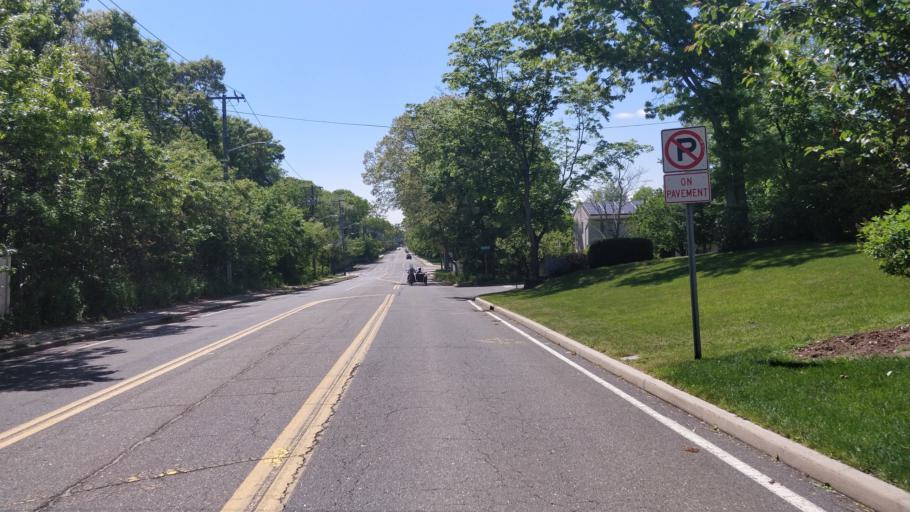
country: US
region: New York
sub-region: Suffolk County
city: Islandia
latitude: 40.8278
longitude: -73.1663
